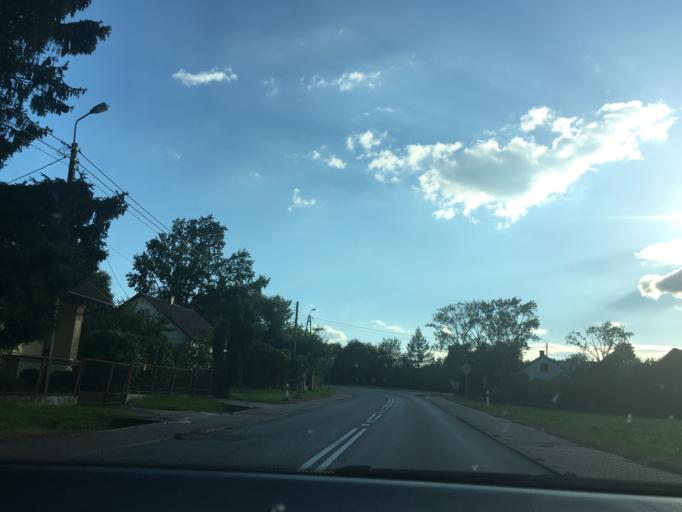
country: PL
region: Masovian Voivodeship
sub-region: Powiat losicki
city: Sarnaki
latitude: 52.3146
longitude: 22.8858
